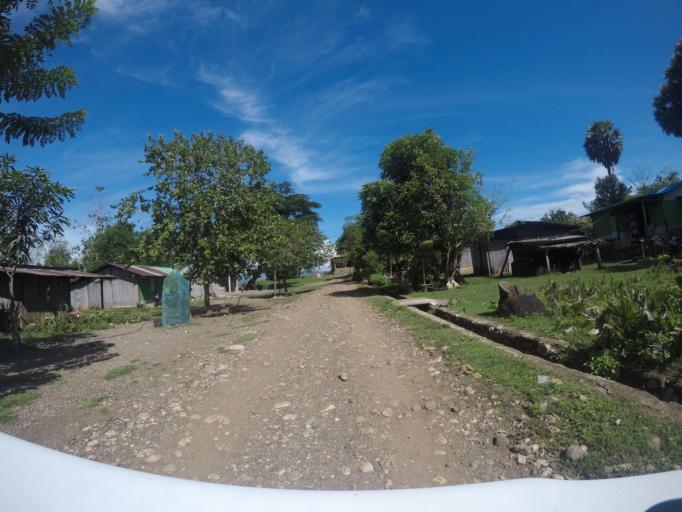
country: TL
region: Bobonaro
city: Maliana
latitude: -8.9839
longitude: 125.1921
